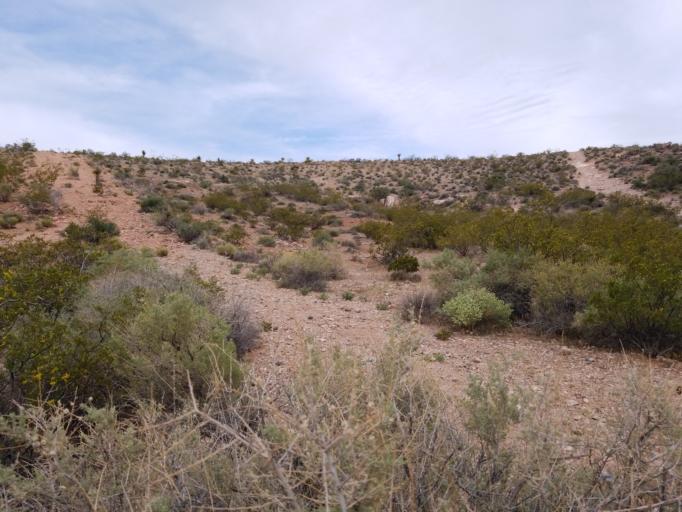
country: US
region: Nevada
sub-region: Clark County
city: Summerlin South
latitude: 36.1443
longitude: -115.4200
